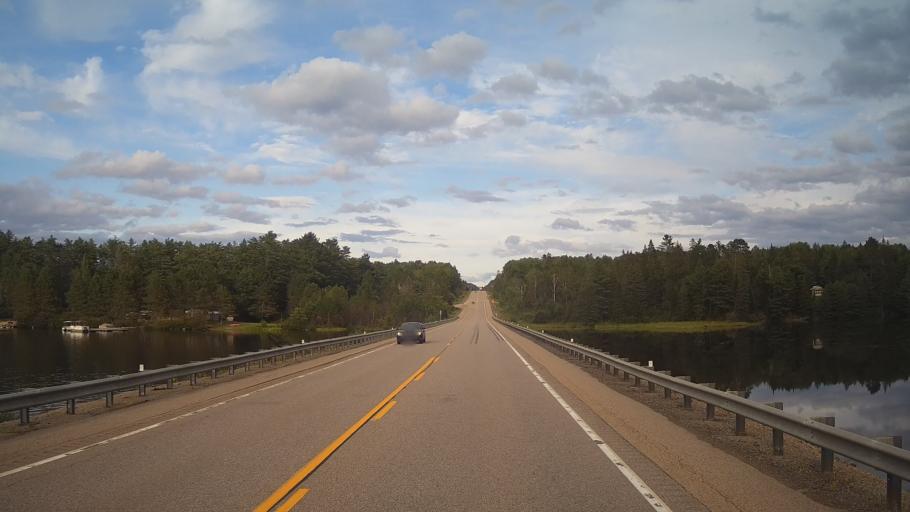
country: CA
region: Ontario
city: Mattawa
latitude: 46.2547
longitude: -78.2787
